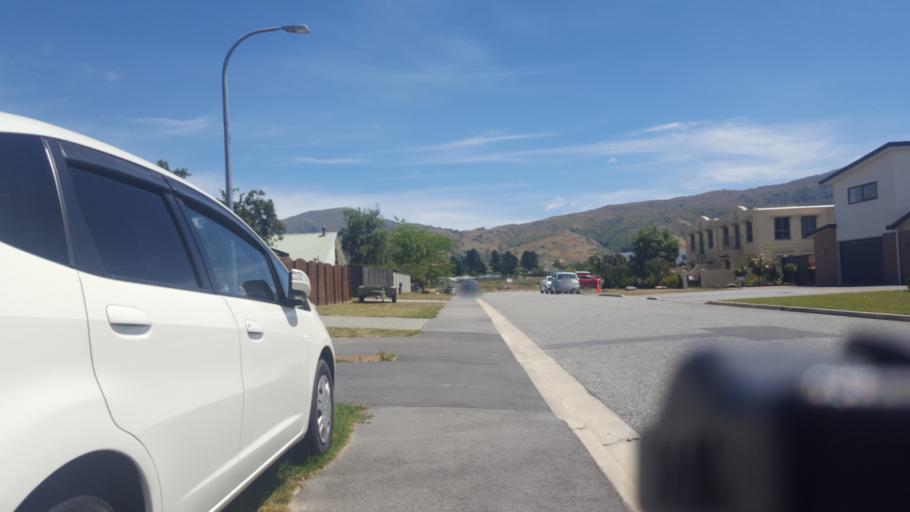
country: NZ
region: Otago
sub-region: Queenstown-Lakes District
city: Wanaka
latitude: -45.0470
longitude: 169.1944
